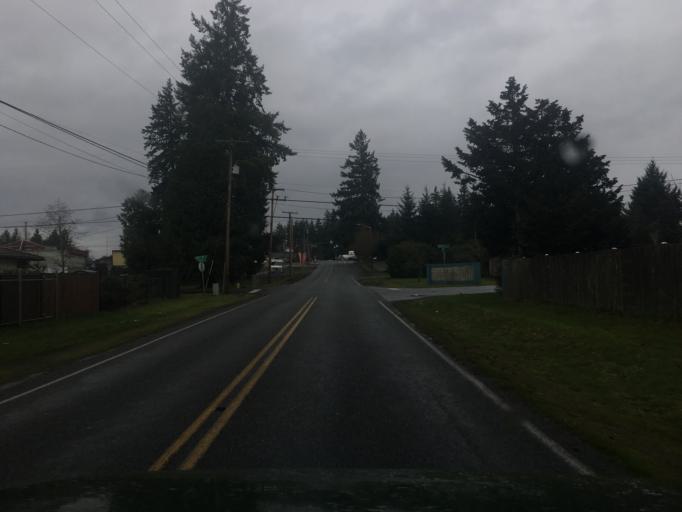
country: US
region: Washington
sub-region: Thurston County
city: Tanglewilde-Thompson Place
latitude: 47.0496
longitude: -122.7913
